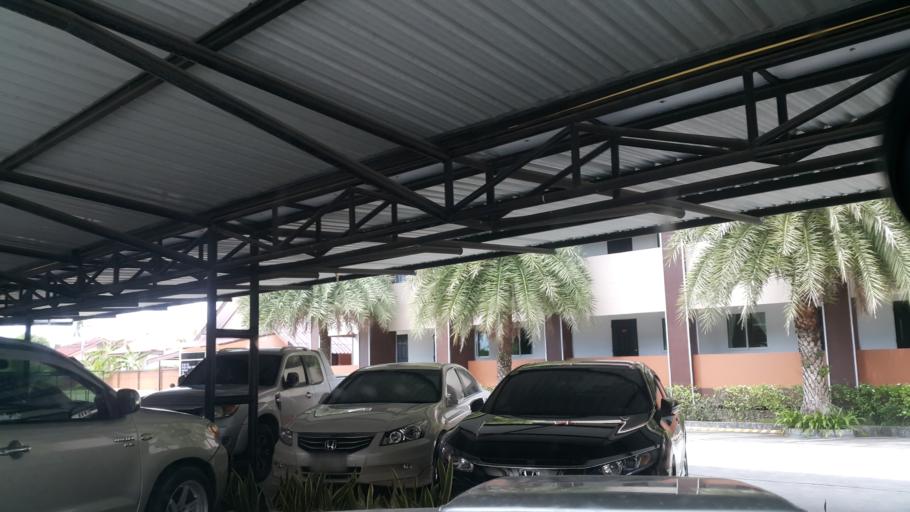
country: TH
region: Rayong
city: Ban Chang
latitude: 12.7204
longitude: 101.0636
